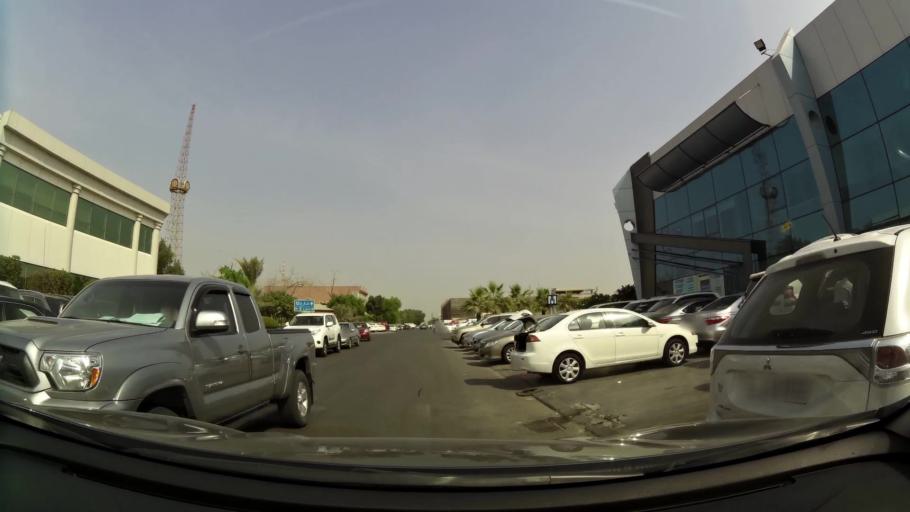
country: KW
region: Al Asimah
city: Ash Shamiyah
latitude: 29.3330
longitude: 47.9421
